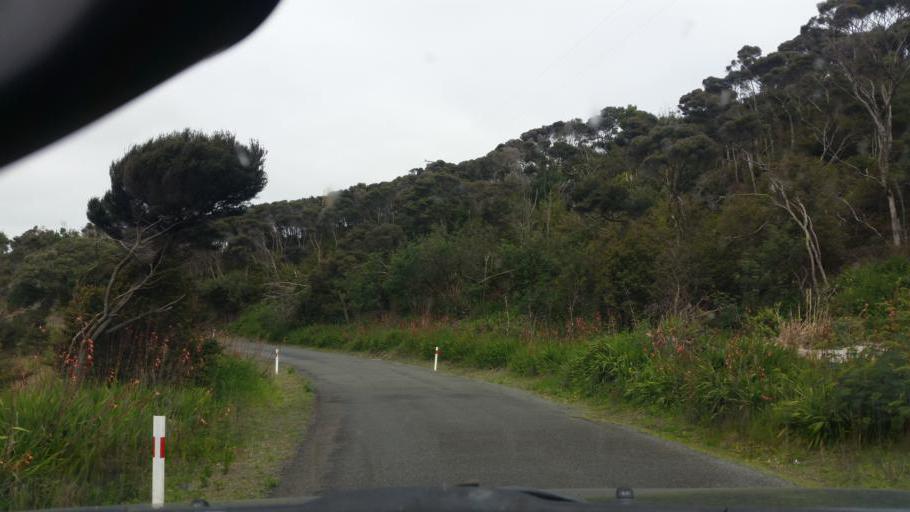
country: NZ
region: Northland
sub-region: Kaipara District
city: Dargaville
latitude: -35.8015
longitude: 173.6273
